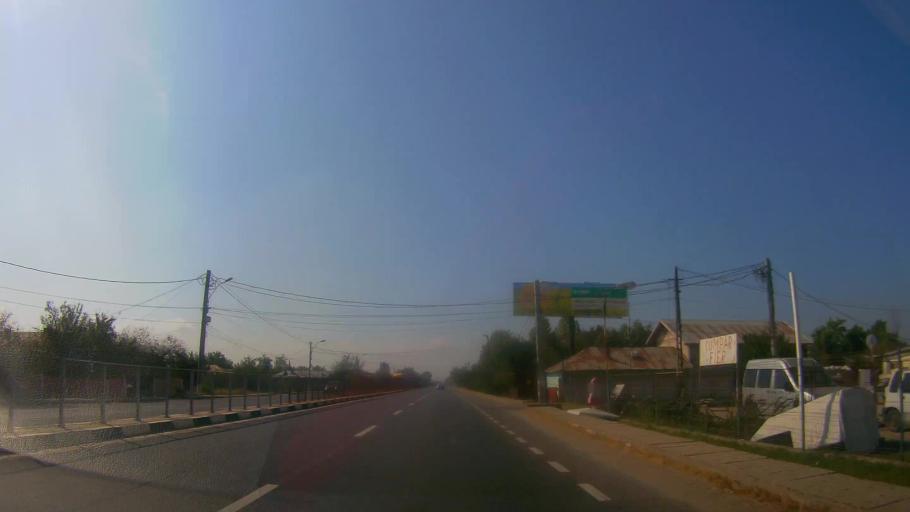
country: RO
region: Giurgiu
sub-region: Comuna Fratesti
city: Remus
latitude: 43.9488
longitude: 25.9804
